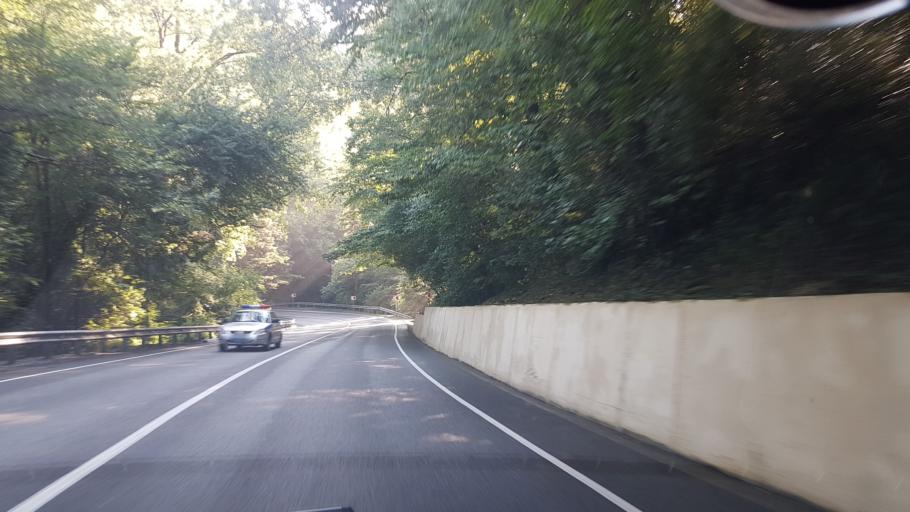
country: RU
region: Krasnodarskiy
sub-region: Sochi City
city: Lazarevskoye
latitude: 43.8251
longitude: 39.4376
